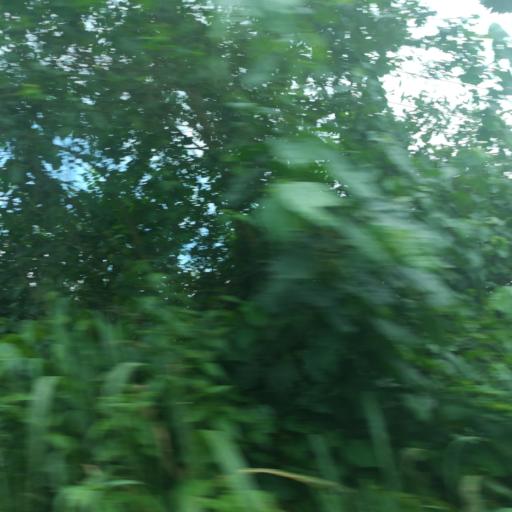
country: NG
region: Lagos
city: Ejirin
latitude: 6.6520
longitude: 3.7190
